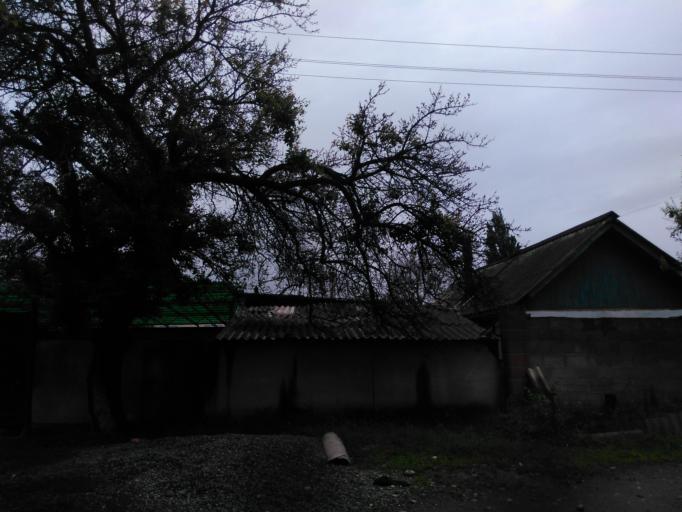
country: KG
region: Chuy
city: Tokmok
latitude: 42.8147
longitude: 75.3241
